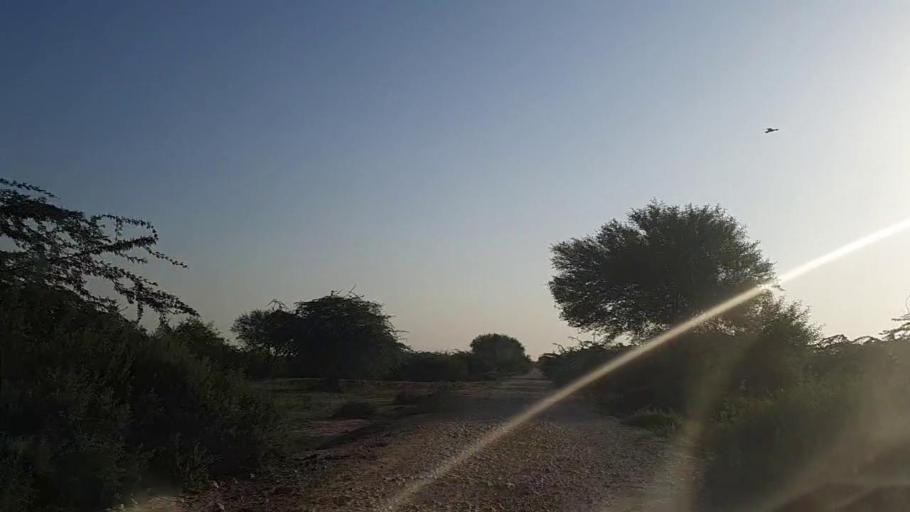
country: PK
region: Sindh
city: Jati
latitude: 24.4274
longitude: 68.1893
